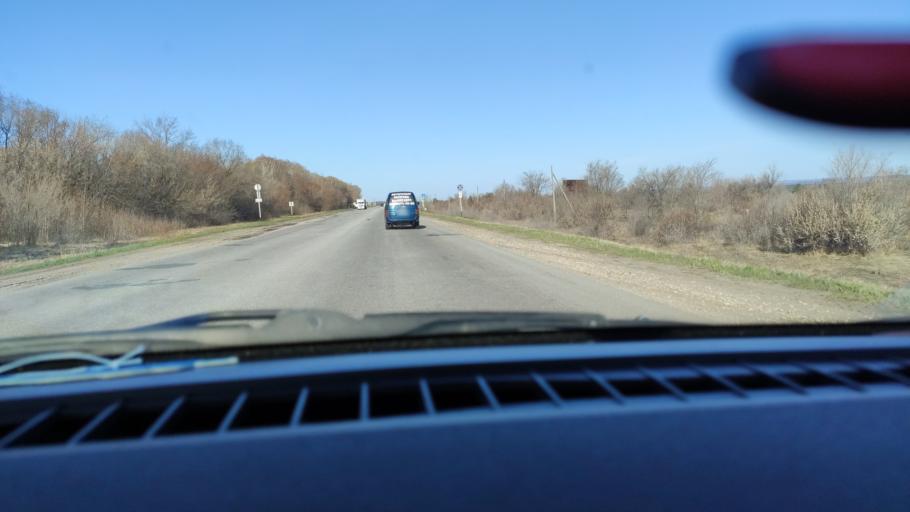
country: RU
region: Samara
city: Varlamovo
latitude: 53.1223
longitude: 48.3111
